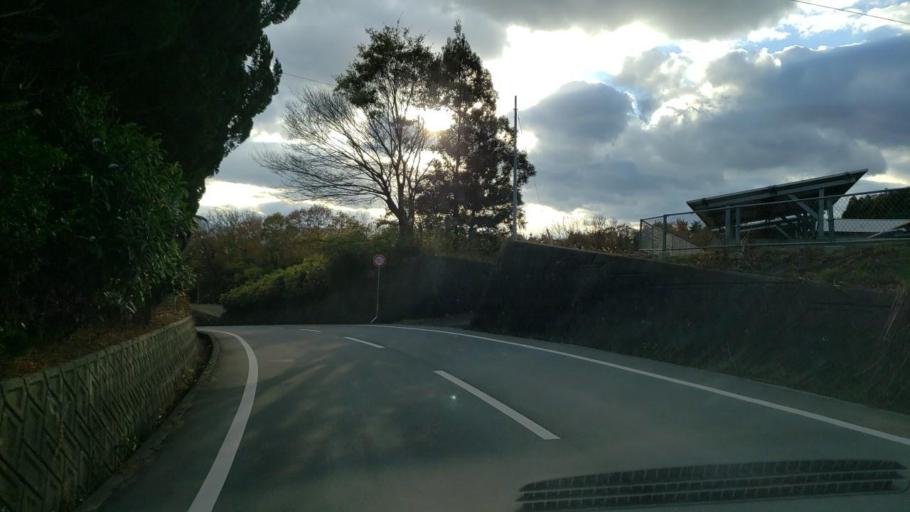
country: JP
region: Tokushima
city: Wakimachi
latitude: 34.0890
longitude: 134.1970
